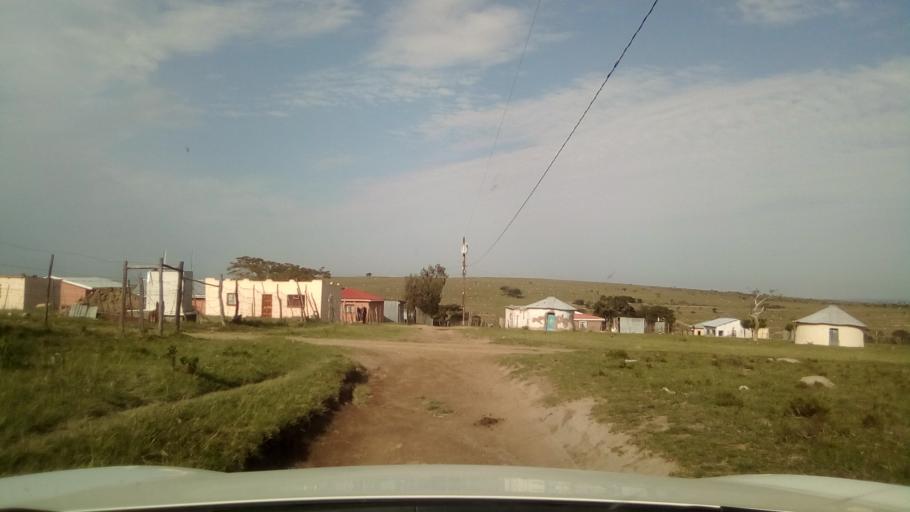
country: ZA
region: Eastern Cape
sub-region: Buffalo City Metropolitan Municipality
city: Bhisho
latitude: -33.0089
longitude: 27.3070
